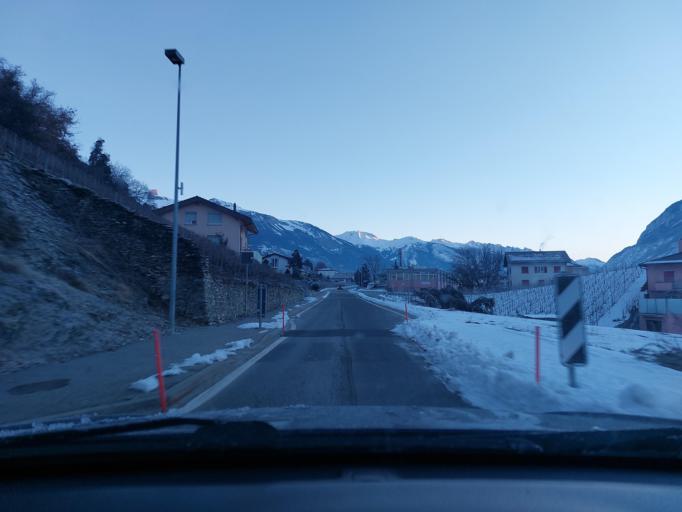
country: CH
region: Valais
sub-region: Sierre District
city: Chalais
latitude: 46.2777
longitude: 7.4990
